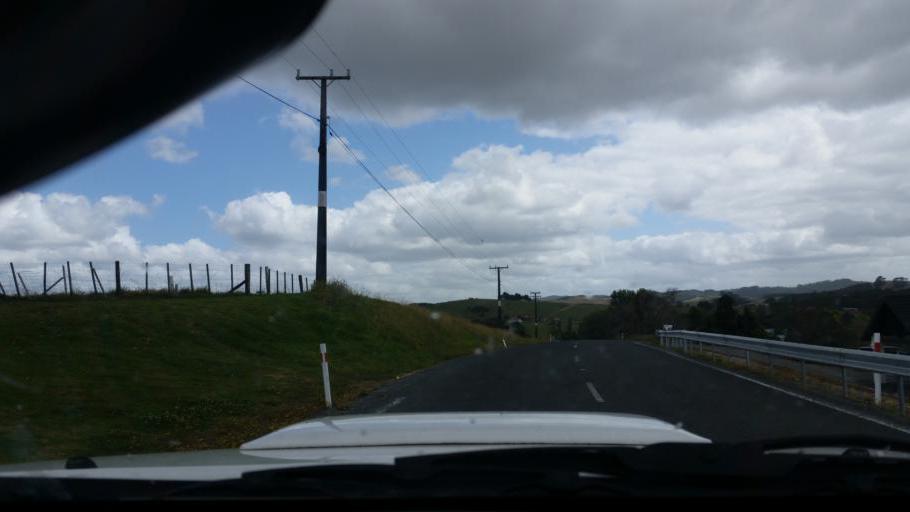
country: NZ
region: Northland
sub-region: Whangarei
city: Ruakaka
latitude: -36.1021
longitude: 174.3510
